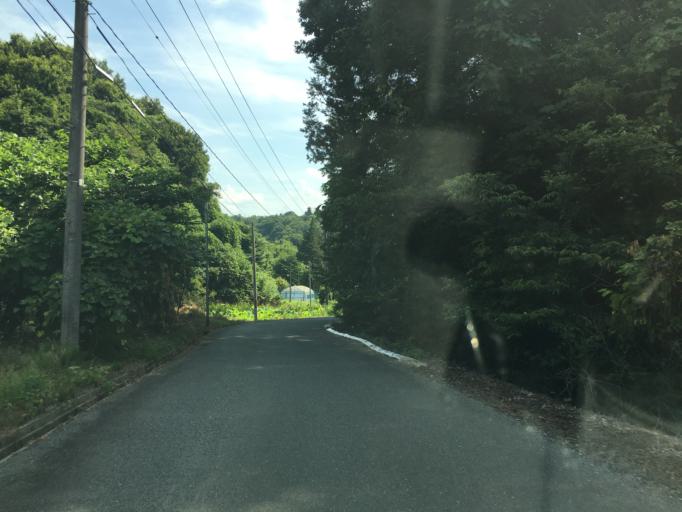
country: JP
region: Fukushima
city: Ishikawa
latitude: 37.1960
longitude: 140.4731
